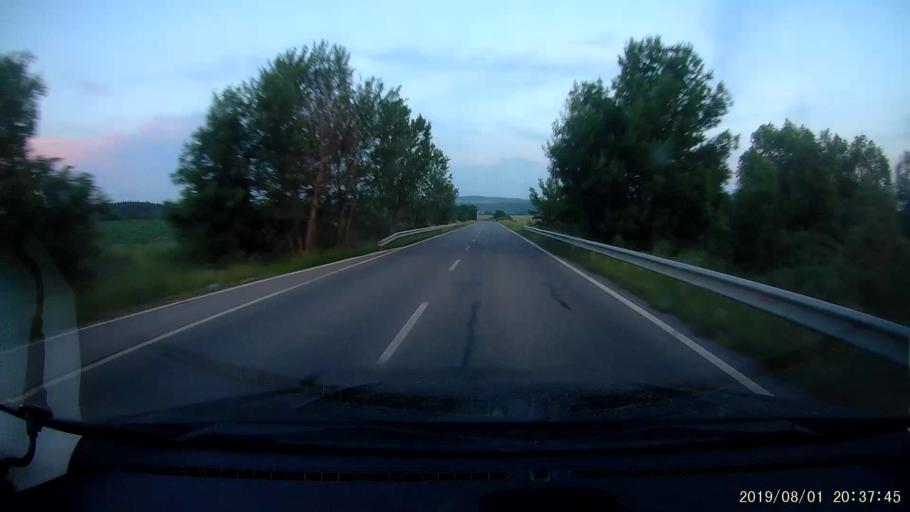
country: BG
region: Yambol
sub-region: Obshtina Elkhovo
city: Elkhovo
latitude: 42.0411
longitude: 26.5956
